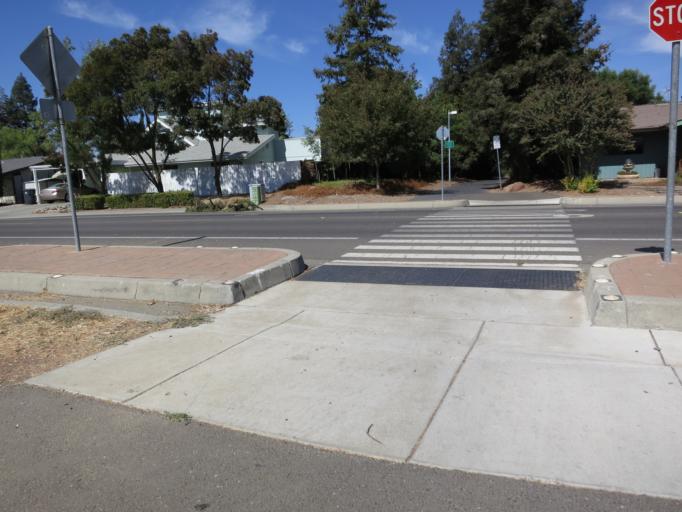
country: US
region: California
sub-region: Yolo County
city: Davis
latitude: 38.5688
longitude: -121.7494
